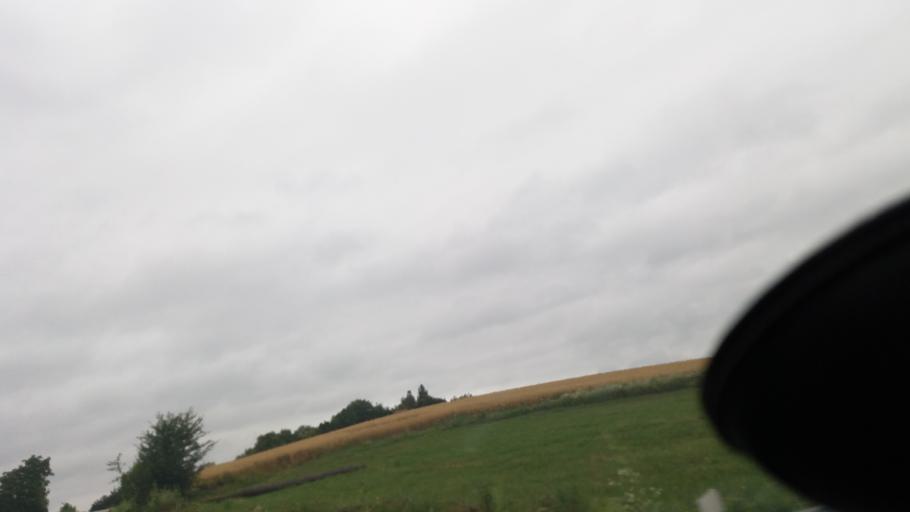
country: RS
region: Central Serbia
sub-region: Kolubarski Okrug
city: Ljig
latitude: 44.2387
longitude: 20.2019
